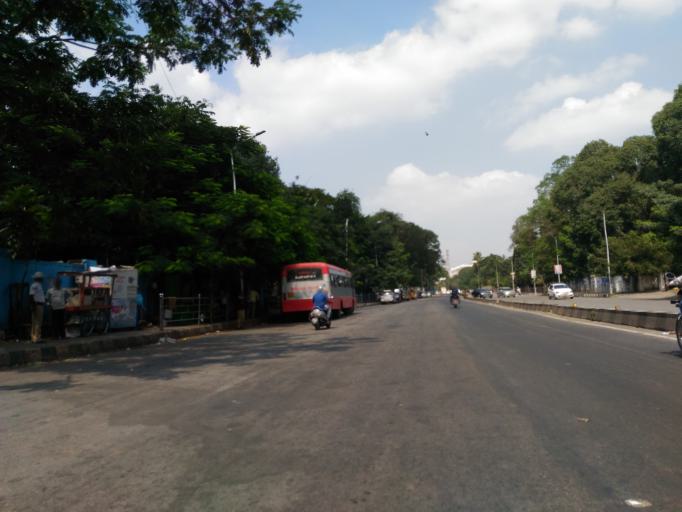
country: IN
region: Karnataka
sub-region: Bangalore Urban
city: Bangalore
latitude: 12.9739
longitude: 77.5815
